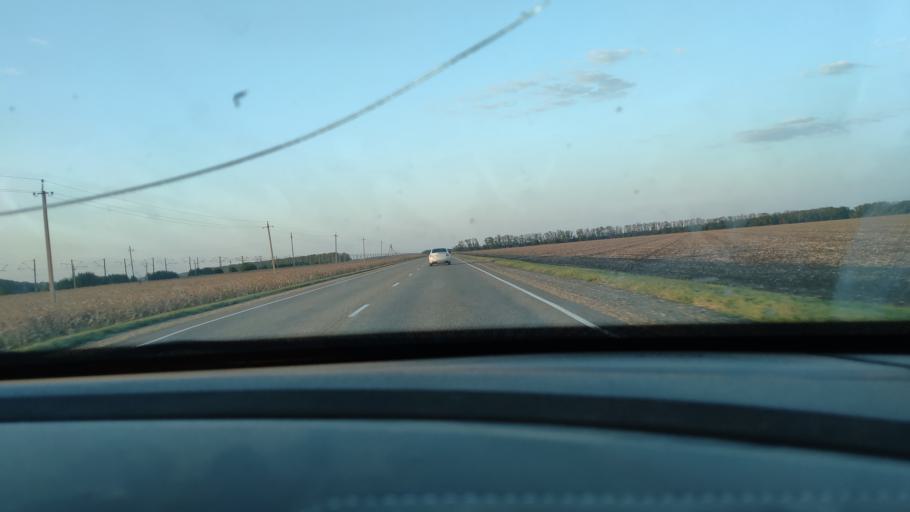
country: RU
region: Krasnodarskiy
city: Novominskaya
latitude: 46.3703
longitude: 38.9750
